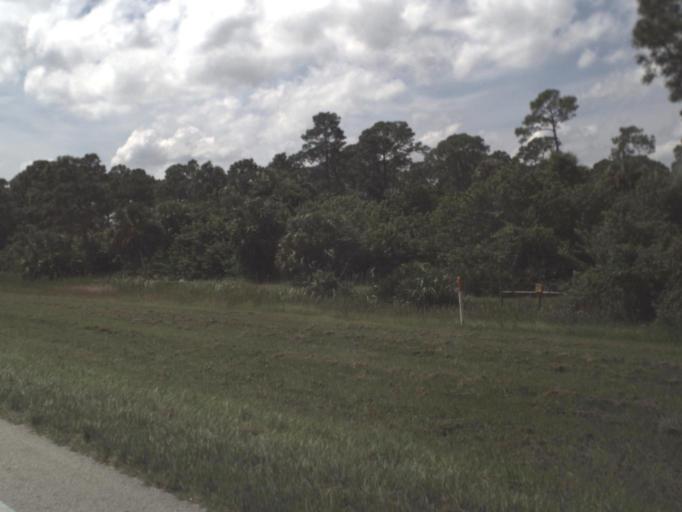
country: US
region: Florida
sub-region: Collier County
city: Immokalee
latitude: 26.4529
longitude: -81.4342
